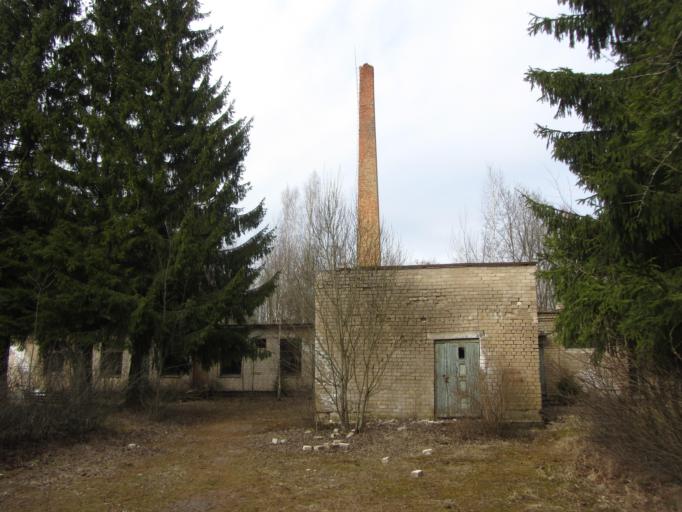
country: LT
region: Utenos apskritis
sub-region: Utena
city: Utena
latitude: 55.4927
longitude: 25.5274
